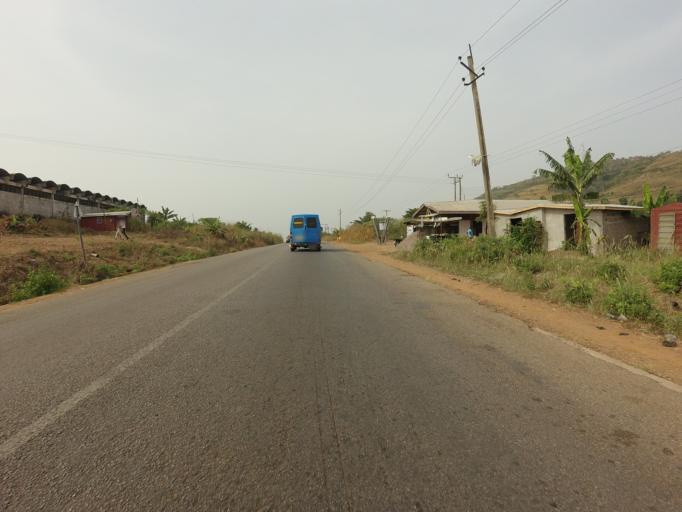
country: GH
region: Volta
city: Ho
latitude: 6.6079
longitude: 0.4552
